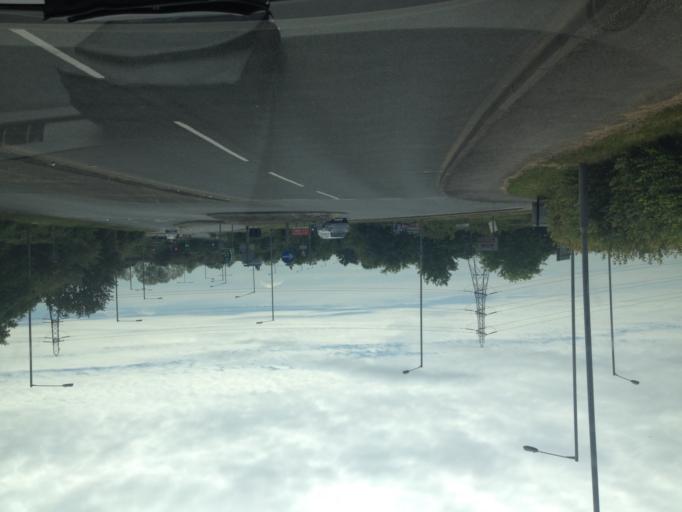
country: GB
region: England
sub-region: Buckinghamshire
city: Denham
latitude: 51.5624
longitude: -0.4952
